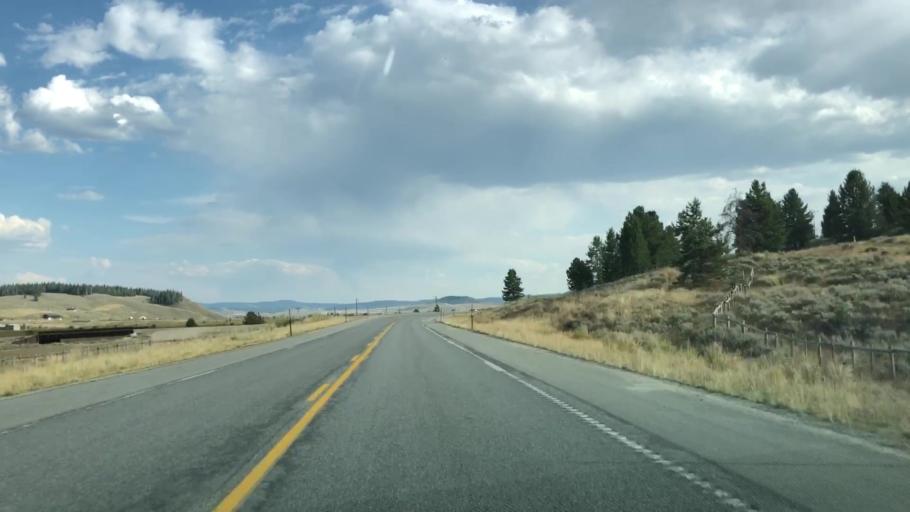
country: US
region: Wyoming
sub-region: Teton County
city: Hoback
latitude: 43.2155
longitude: -110.4201
